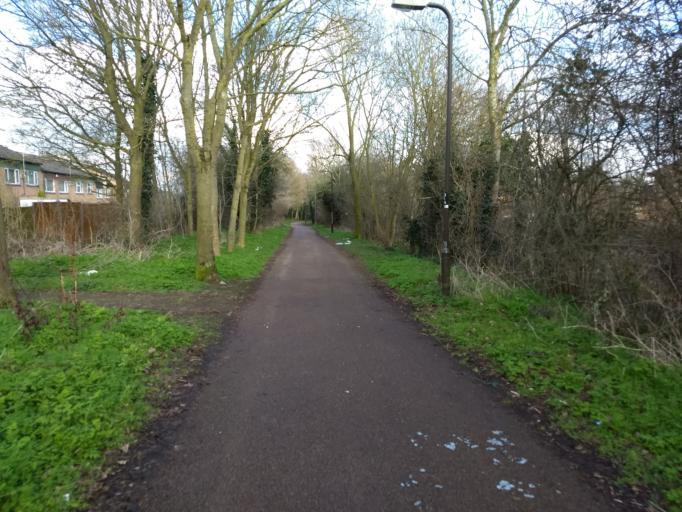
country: GB
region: England
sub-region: Milton Keynes
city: Milton Keynes
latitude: 52.0285
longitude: -0.7415
